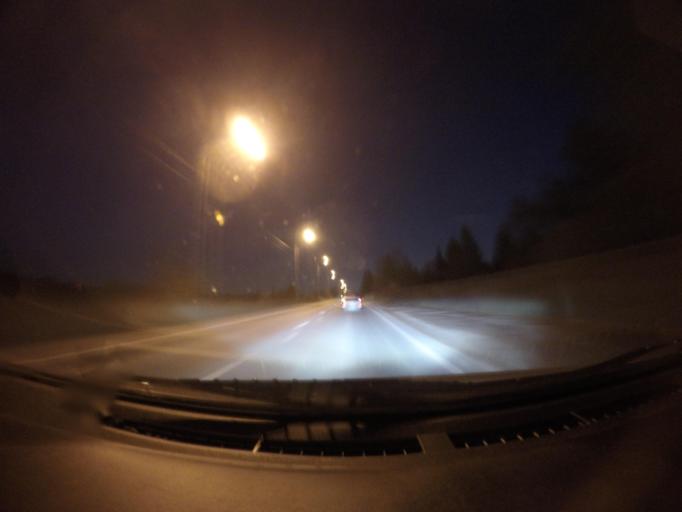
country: RU
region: Moskovskaya
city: Novopodrezkovo
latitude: 55.9293
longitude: 37.3583
